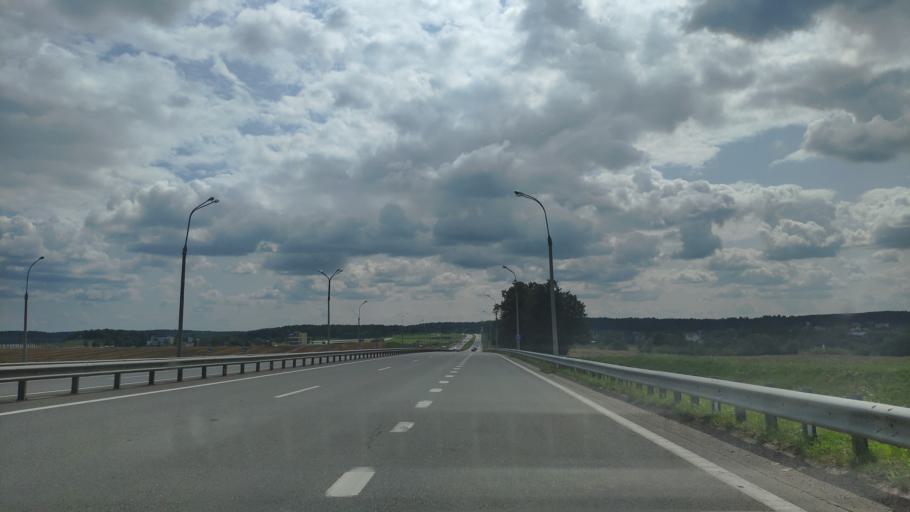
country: BY
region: Minsk
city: Zaslawye
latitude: 54.0059
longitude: 27.3089
